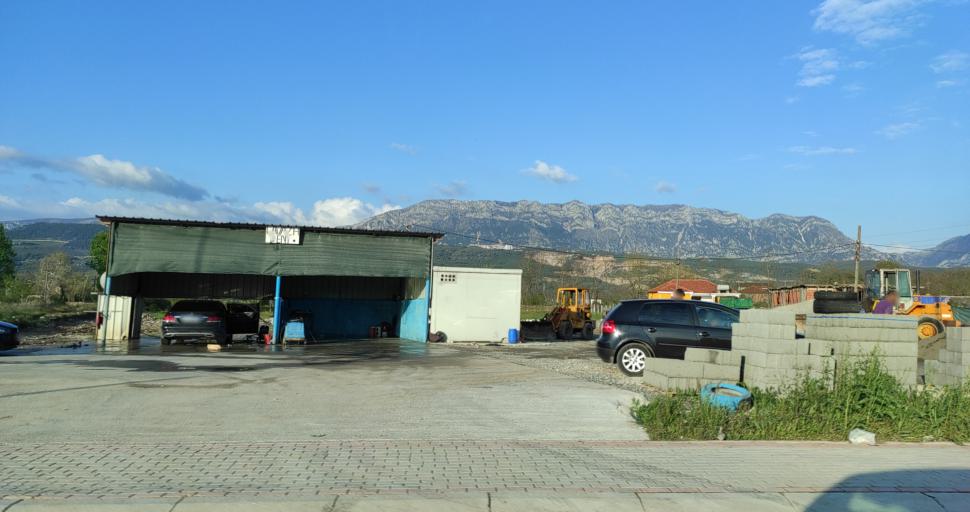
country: AL
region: Durres
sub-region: Rrethi i Krujes
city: Fushe-Kruje
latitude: 41.4883
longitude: 19.7253
